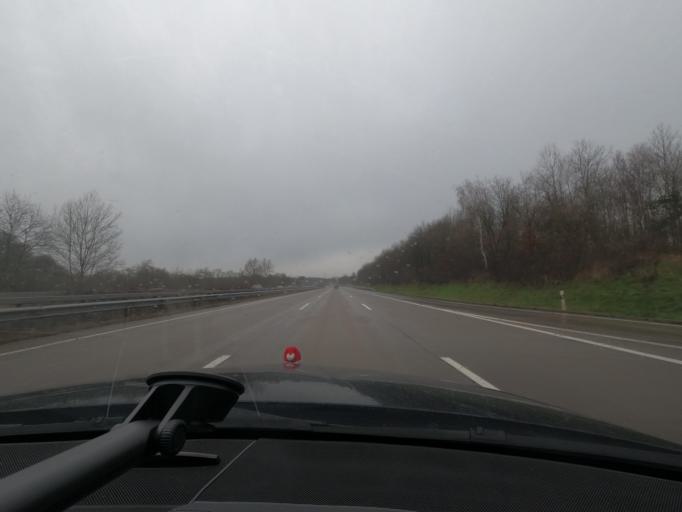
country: DE
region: Lower Saxony
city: Brackel
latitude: 53.3067
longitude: 10.0721
